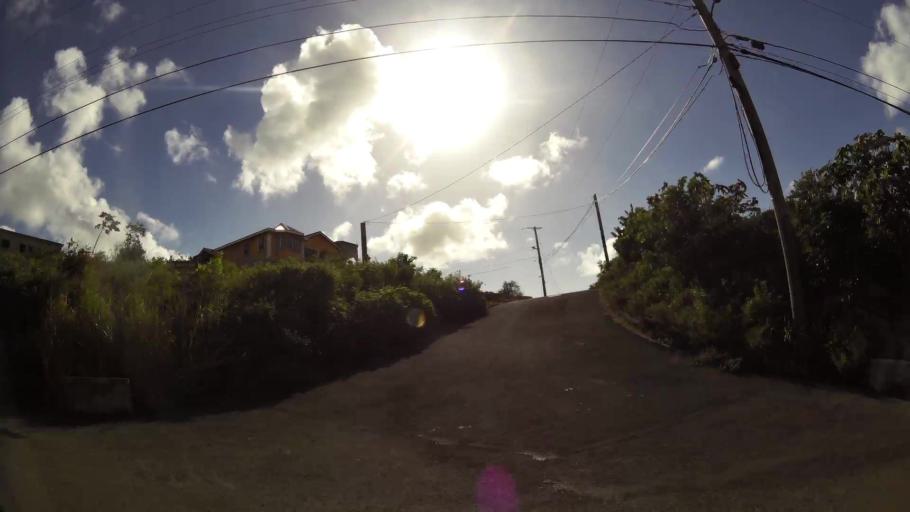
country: LC
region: Castries Quarter
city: Bisee
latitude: 14.0406
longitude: -60.9575
